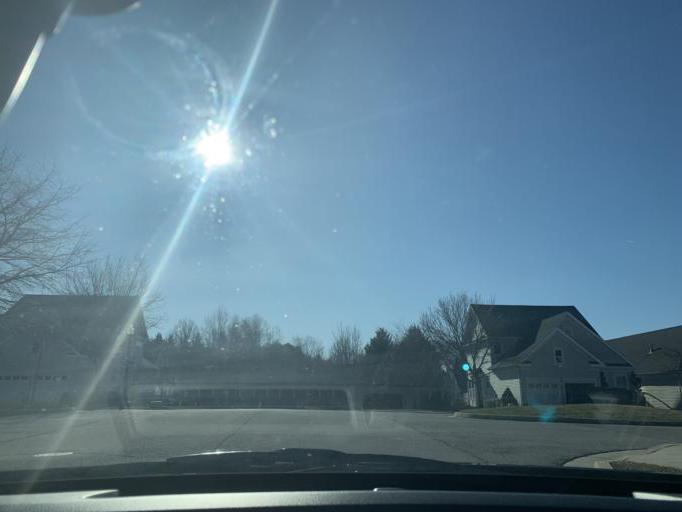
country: US
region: Maryland
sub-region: Baltimore County
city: Garrison
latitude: 39.3969
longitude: -76.7408
